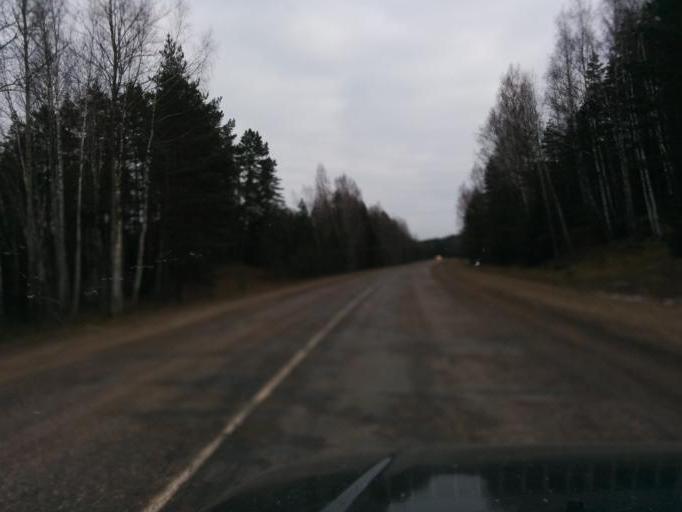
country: LV
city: Tireli
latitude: 56.8606
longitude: 23.5374
